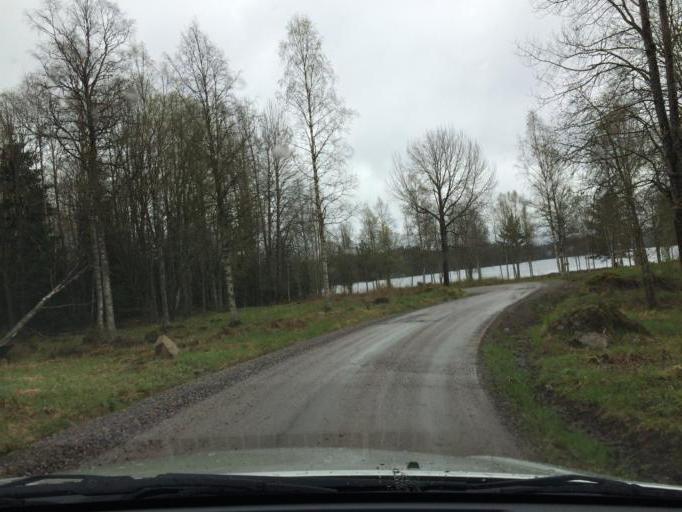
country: SE
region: Dalarna
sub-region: Ludvika Kommun
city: Abborrberget
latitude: 60.0225
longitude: 14.6259
